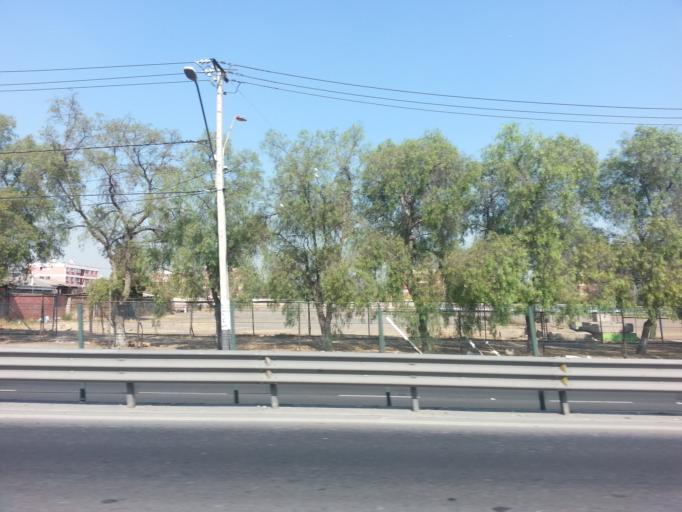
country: CL
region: Santiago Metropolitan
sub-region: Provincia de Santiago
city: La Pintana
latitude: -33.5403
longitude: -70.6499
